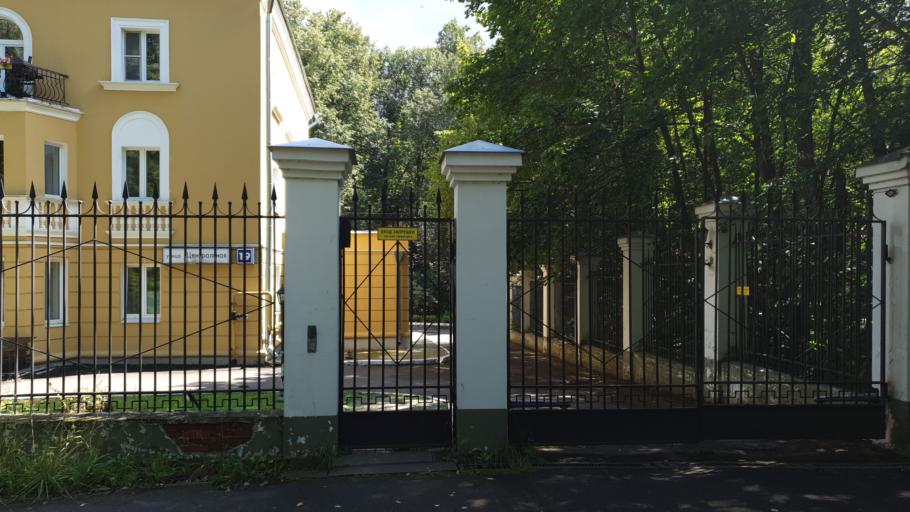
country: RU
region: Moskovskaya
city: Gorki-Leninskiye
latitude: 55.5035
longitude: 37.7717
